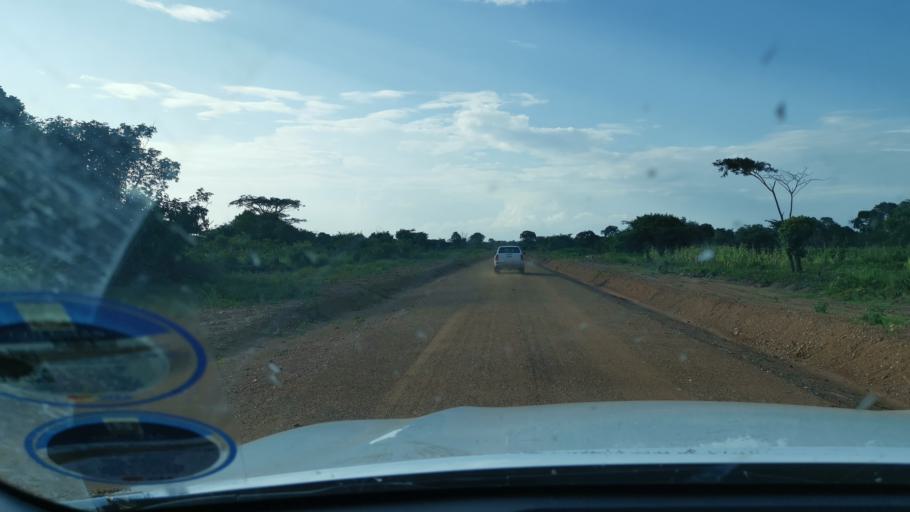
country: ZM
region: Luapula
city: Samfya
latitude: -11.1155
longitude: 29.5782
